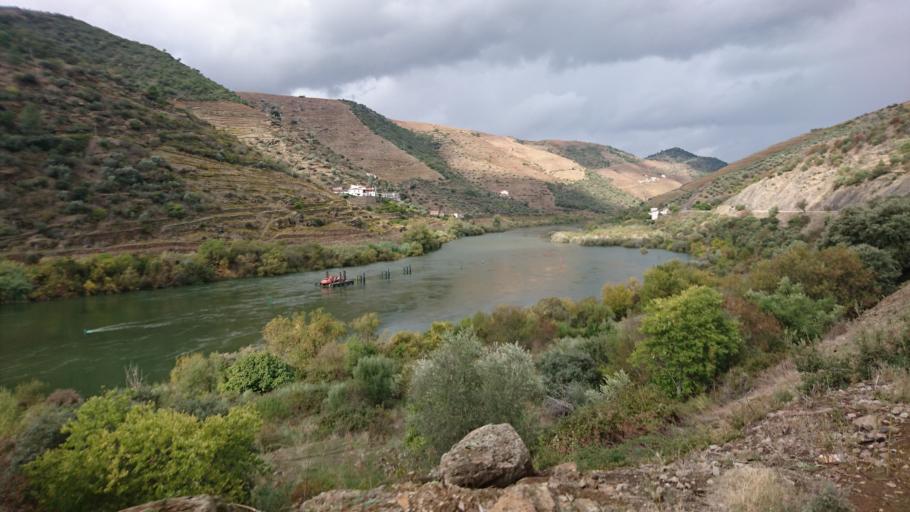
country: PT
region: Viseu
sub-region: Sao Joao da Pesqueira
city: Sao Joao da Pesqueira
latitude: 41.1714
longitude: -7.3718
